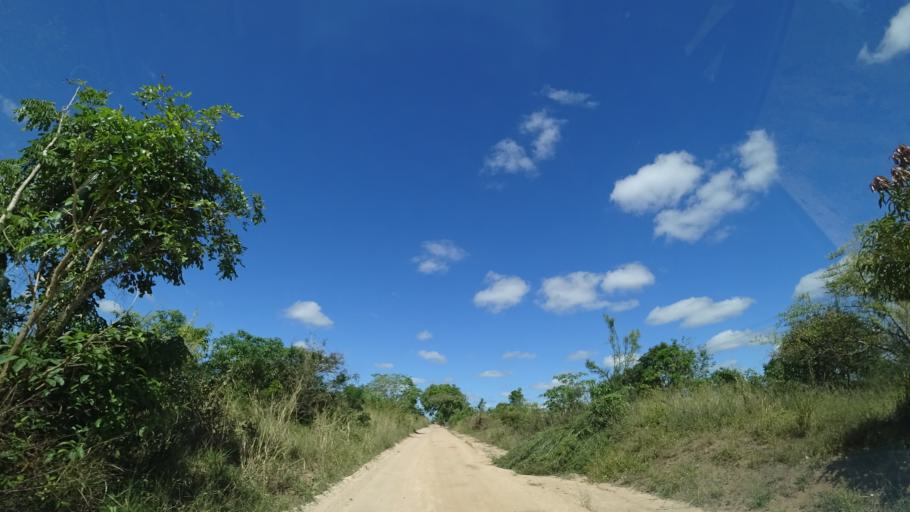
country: MZ
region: Sofala
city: Dondo
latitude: -19.3189
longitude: 34.6911
